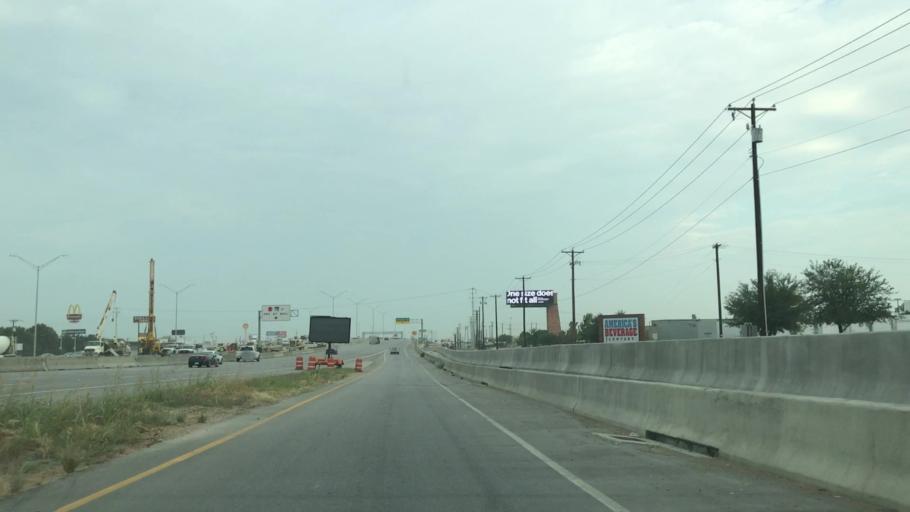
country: US
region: Texas
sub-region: Dallas County
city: Irving
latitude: 32.8375
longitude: -96.9255
